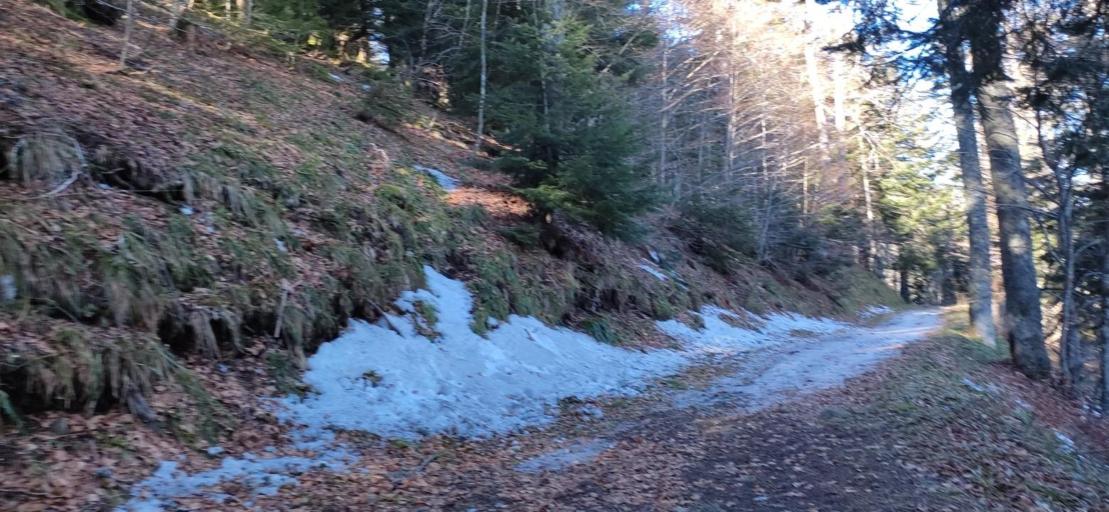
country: FR
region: Auvergne
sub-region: Departement du Puy-de-Dome
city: Mont-Dore
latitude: 45.5609
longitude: 2.8075
